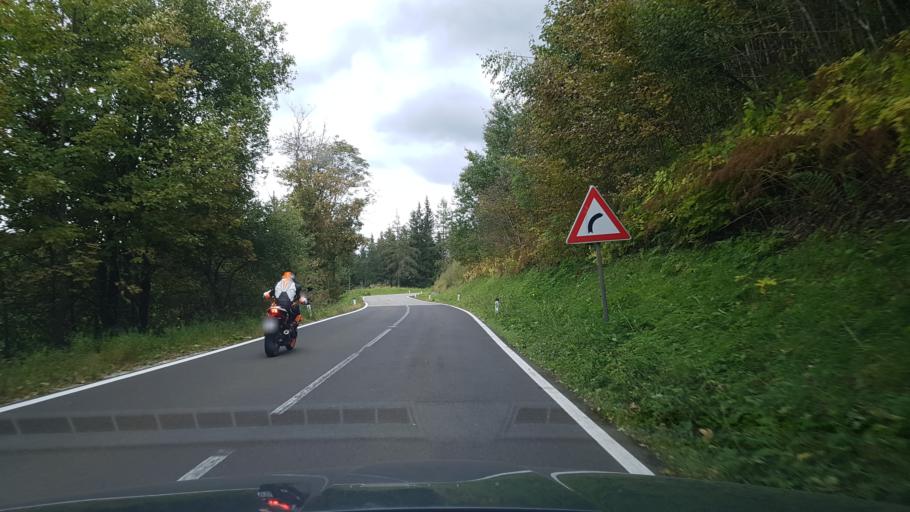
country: AT
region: Styria
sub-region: Politischer Bezirk Murtal
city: Kleinlobming
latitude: 47.1364
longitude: 14.8568
